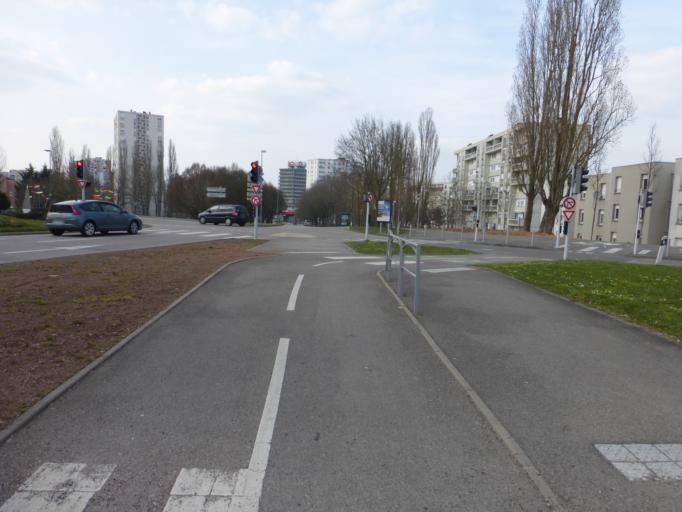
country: FR
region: Lorraine
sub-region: Departement de Meurthe-et-Moselle
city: Vandoeuvre-les-Nancy
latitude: 48.6582
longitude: 6.1779
